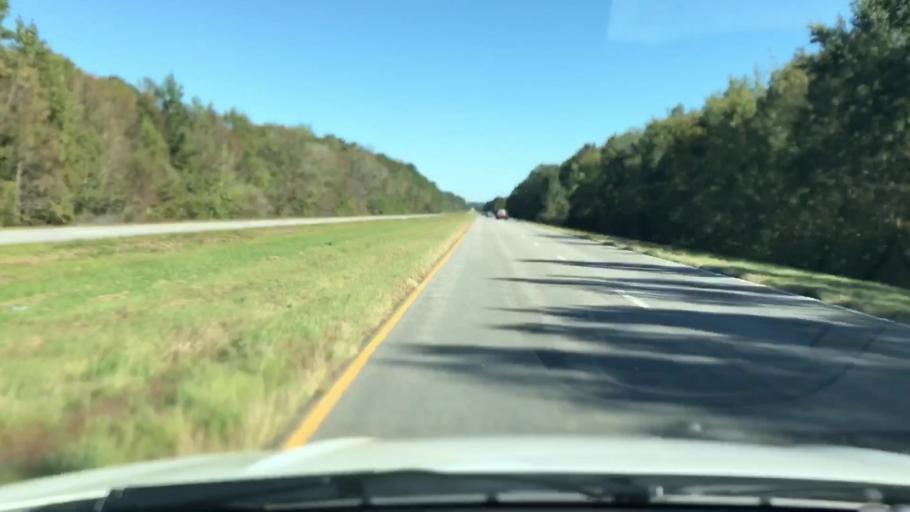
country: US
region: South Carolina
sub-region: Charleston County
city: Ravenel
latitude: 32.7614
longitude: -80.4137
